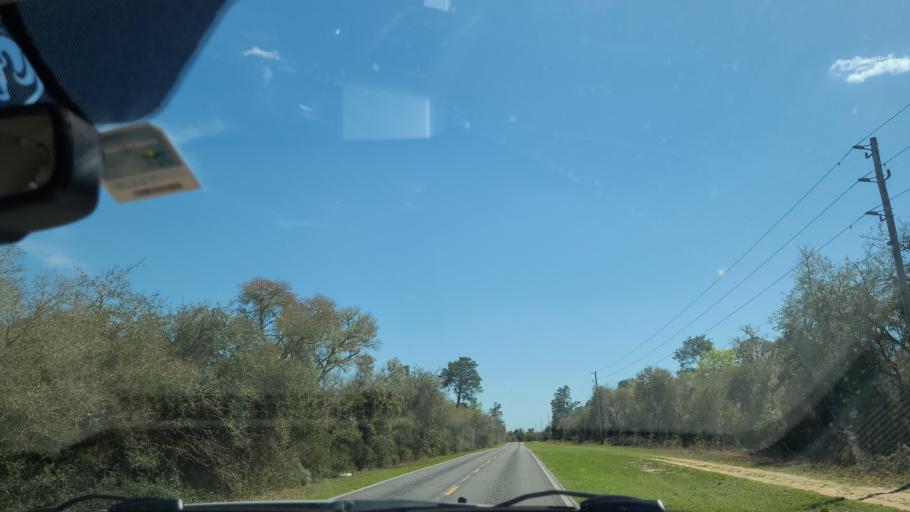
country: US
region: Florida
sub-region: Marion County
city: Citra
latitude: 29.4224
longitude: -81.9138
